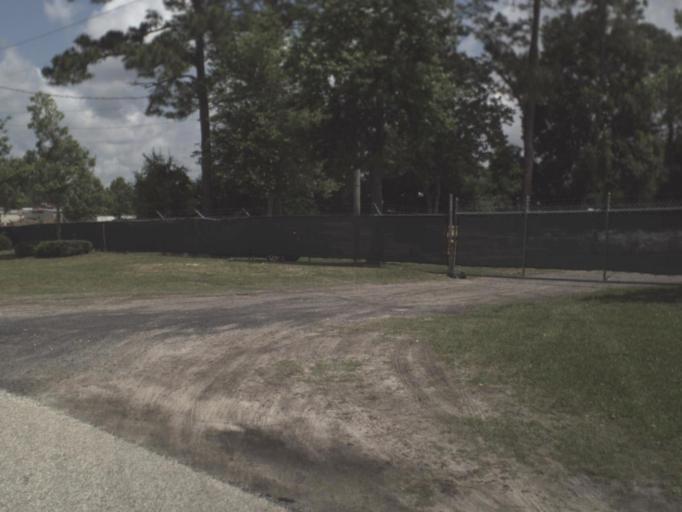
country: US
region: Florida
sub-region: Saint Johns County
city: Palm Valley
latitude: 30.0850
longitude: -81.4588
